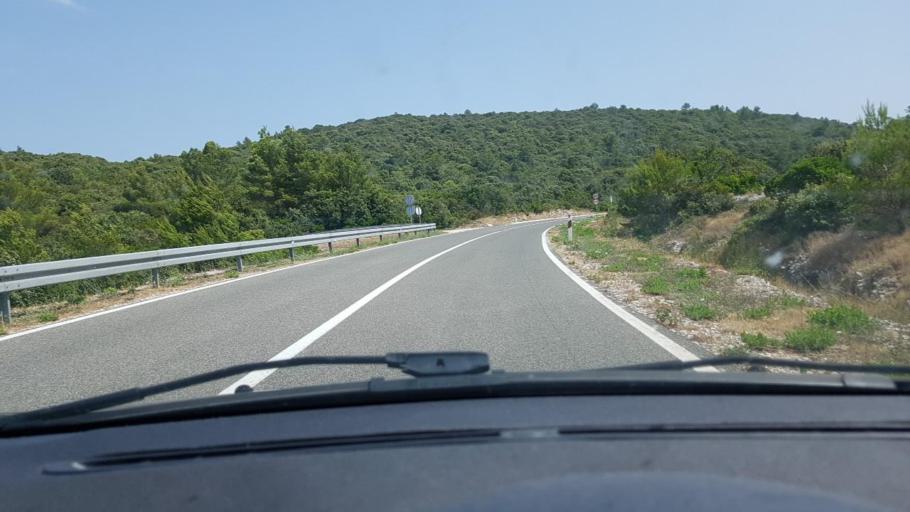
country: HR
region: Dubrovacko-Neretvanska
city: Smokvica
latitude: 42.9562
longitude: 16.9415
